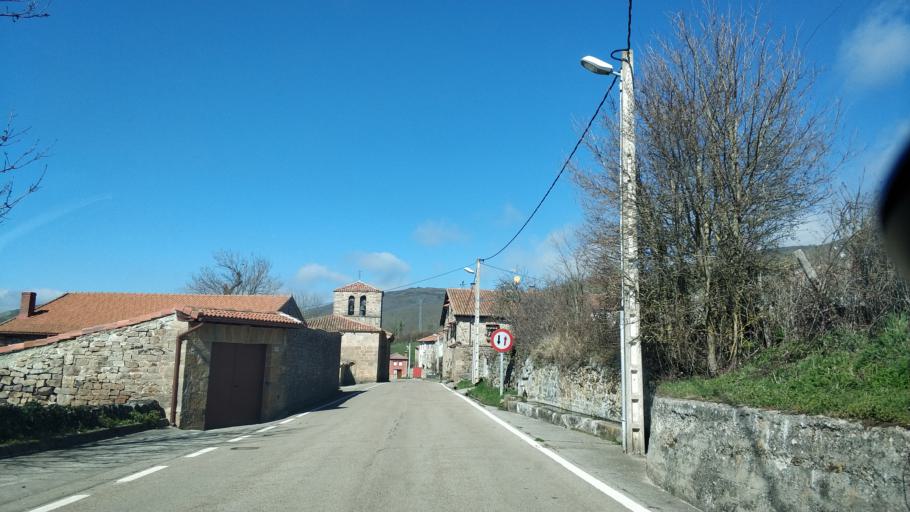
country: ES
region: Cantabria
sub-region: Provincia de Cantabria
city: Mataporquera
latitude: 42.9081
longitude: -4.0669
